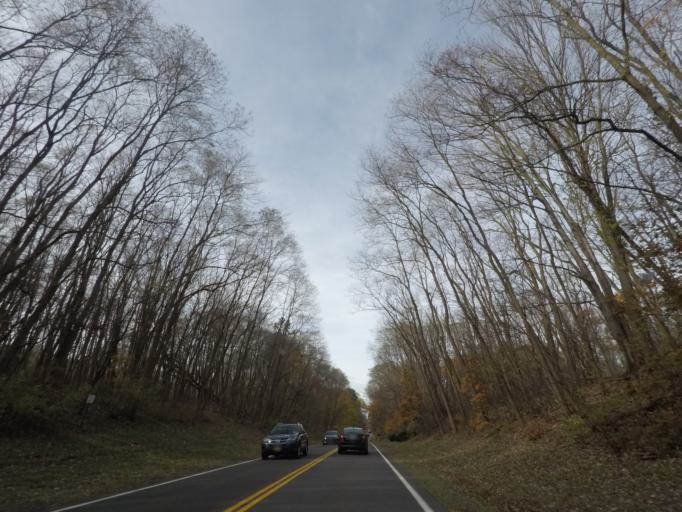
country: US
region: New York
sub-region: Albany County
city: Westmere
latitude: 42.7282
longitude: -73.8982
